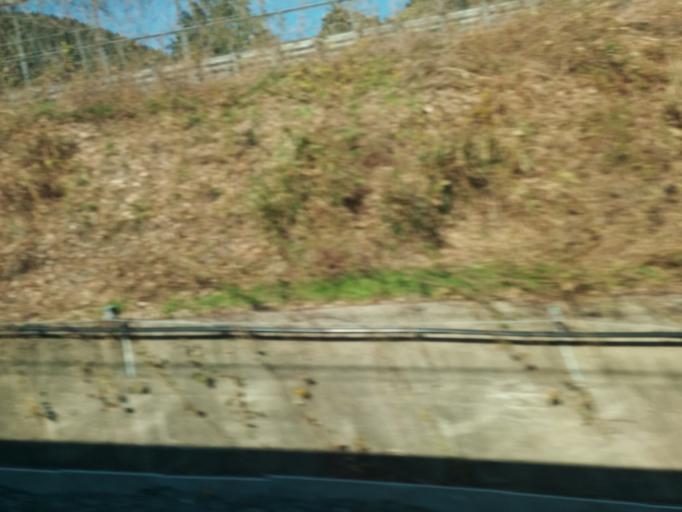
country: JP
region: Aichi
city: Gamagori
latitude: 34.8154
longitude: 137.2667
